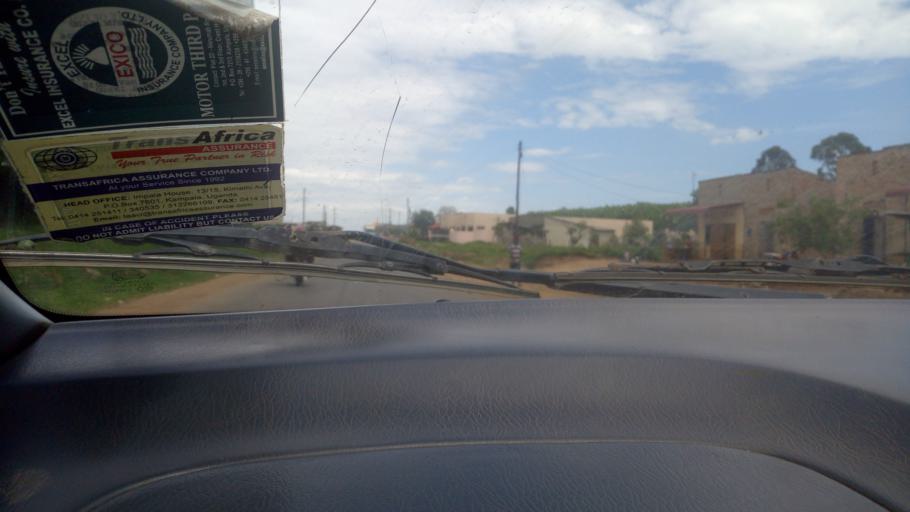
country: UG
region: Western Region
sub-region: Mbarara District
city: Bwizibwera
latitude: -0.4107
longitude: 30.5687
